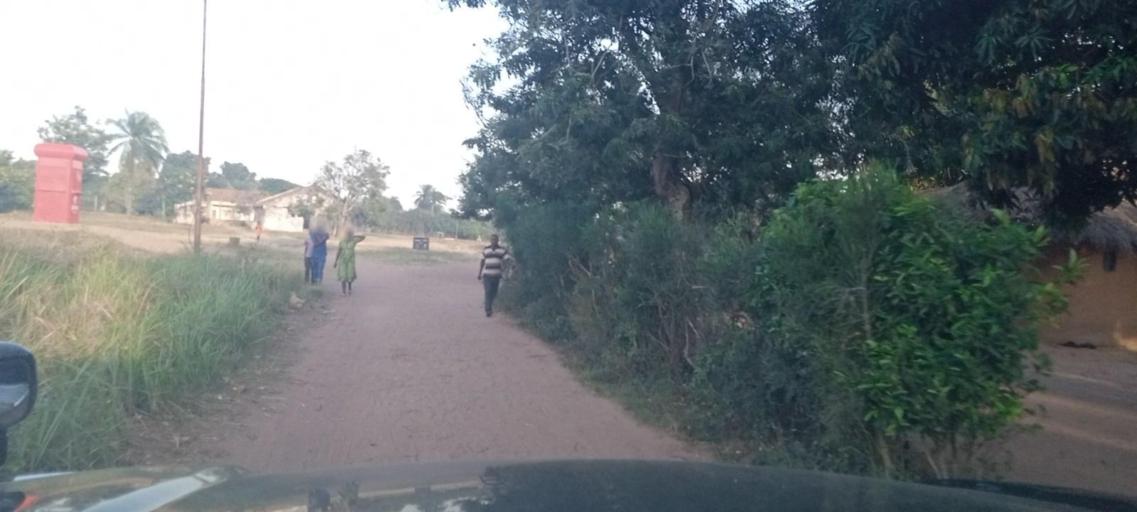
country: CD
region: Kasai-Oriental
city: Lubao
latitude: -5.3851
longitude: 25.7426
